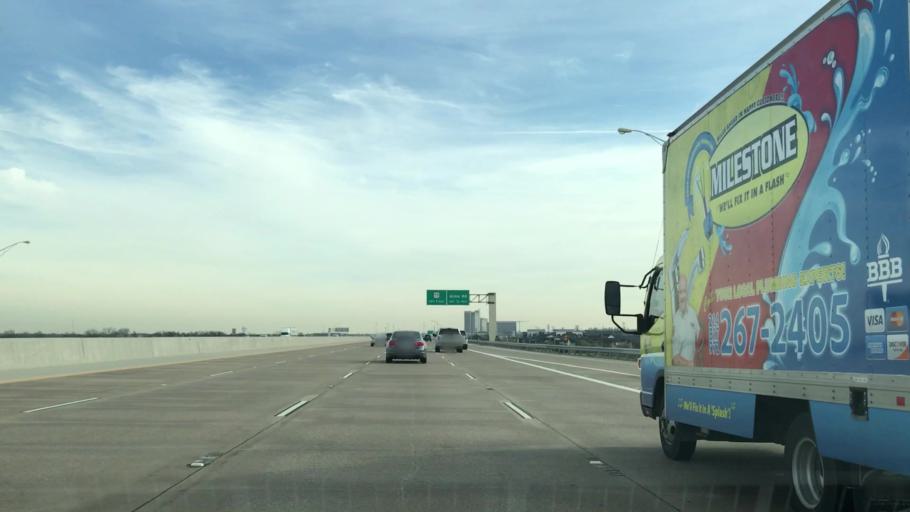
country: US
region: Texas
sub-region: Collin County
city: Plano
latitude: 33.0037
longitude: -96.7355
